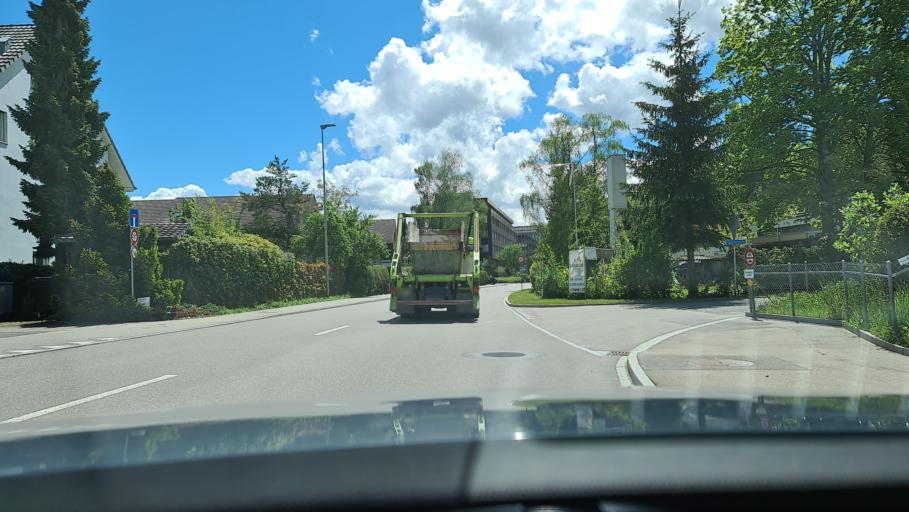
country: CH
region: Zurich
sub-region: Bezirk Horgen
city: Ruschlikon
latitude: 47.3047
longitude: 8.5441
